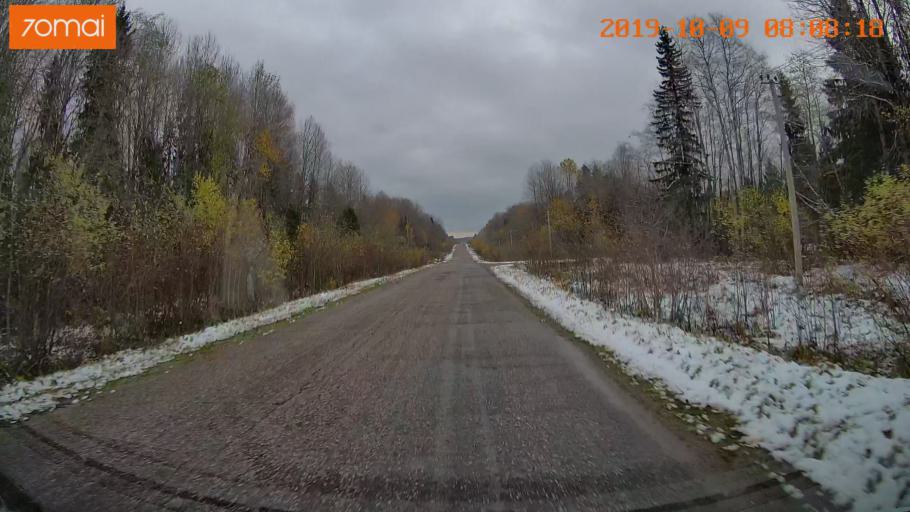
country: RU
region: Jaroslavl
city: Kukoboy
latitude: 58.7034
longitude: 40.0934
